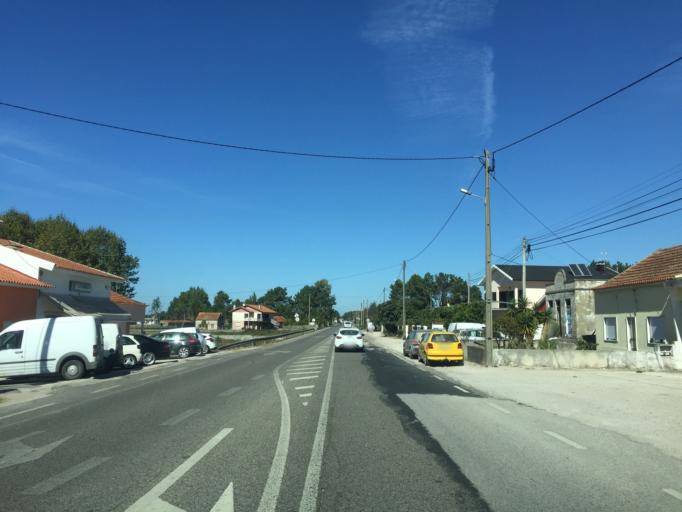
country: PT
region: Coimbra
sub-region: Figueira da Foz
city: Alhadas
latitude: 40.2578
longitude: -8.7797
